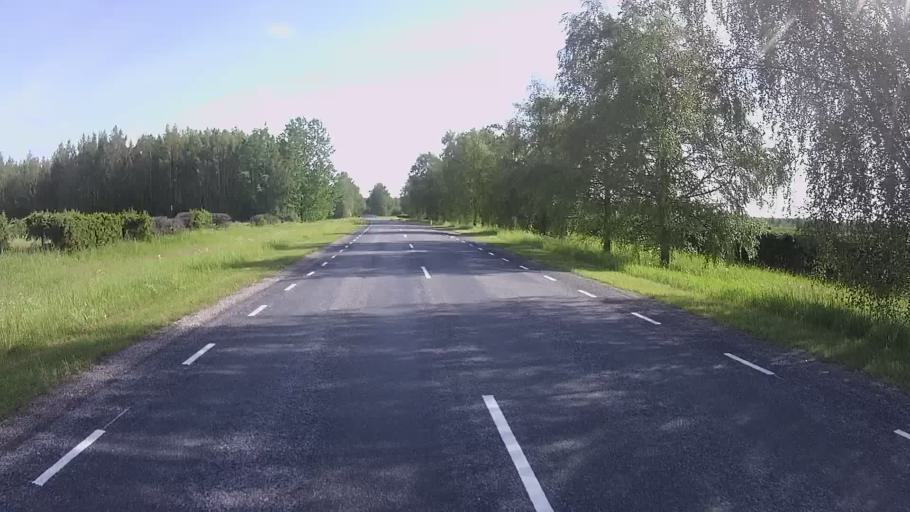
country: EE
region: Valgamaa
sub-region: Torva linn
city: Torva
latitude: 58.0677
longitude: 26.0312
